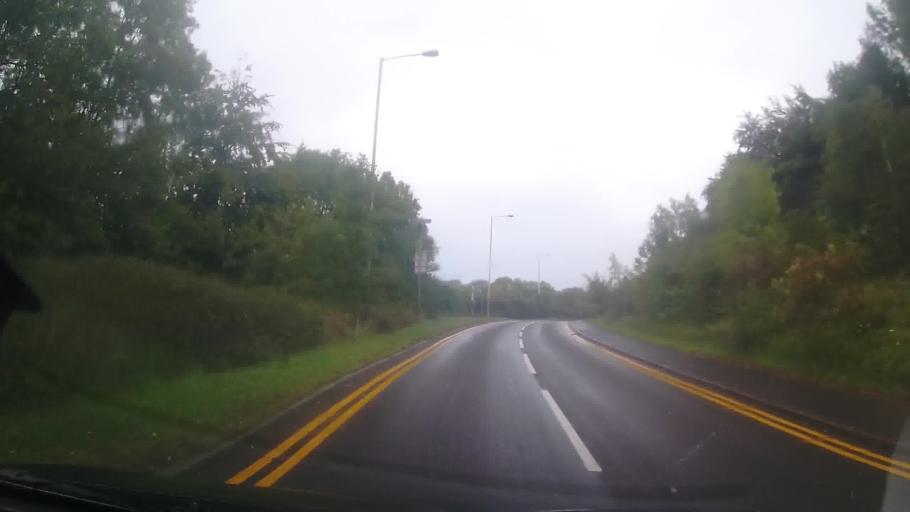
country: GB
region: England
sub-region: Shropshire
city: Much Wenlock
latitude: 52.6046
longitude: -2.5569
